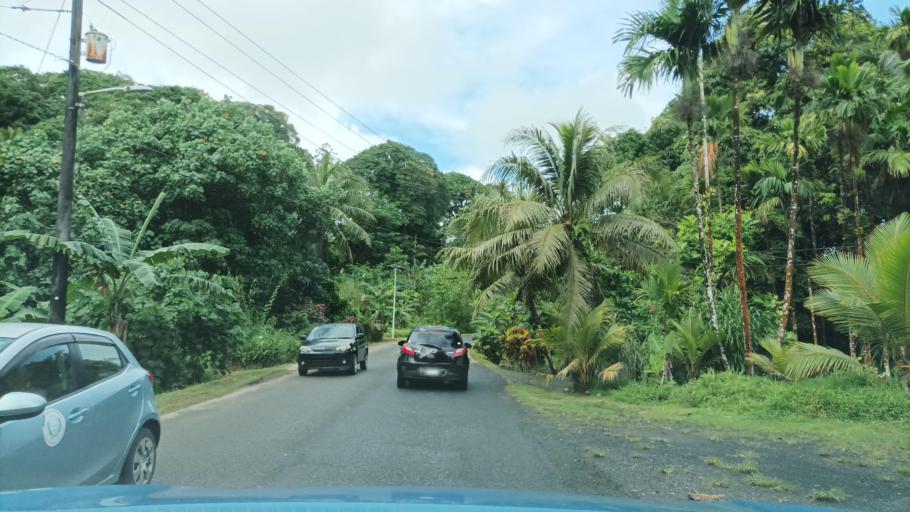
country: FM
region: Pohnpei
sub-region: Kolonia Municipality
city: Kolonia
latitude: 6.9544
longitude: 158.2452
